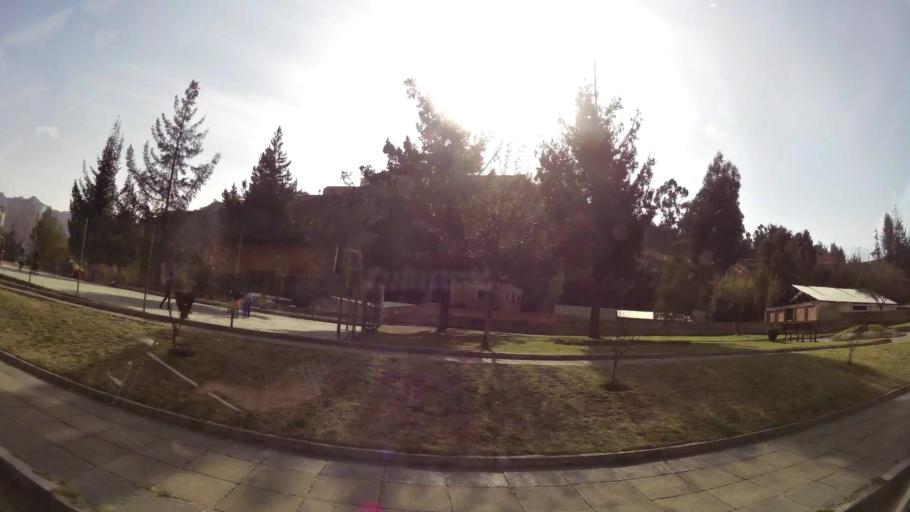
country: BO
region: La Paz
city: La Paz
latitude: -16.5346
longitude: -68.0774
